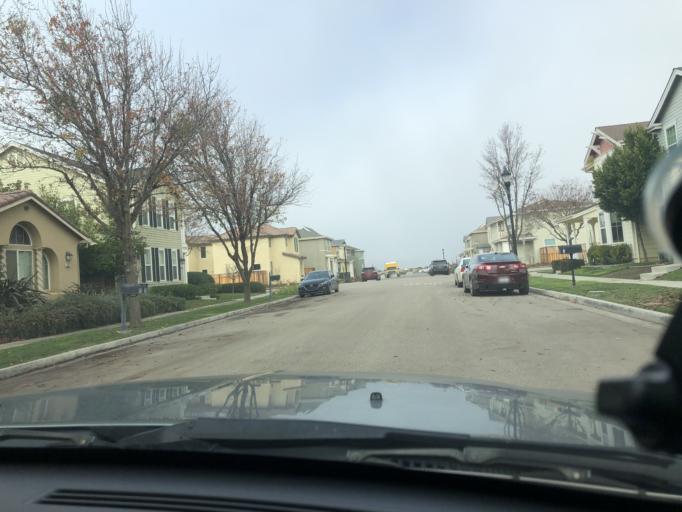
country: US
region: California
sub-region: Monterey County
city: King City
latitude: 36.2208
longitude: -121.1308
